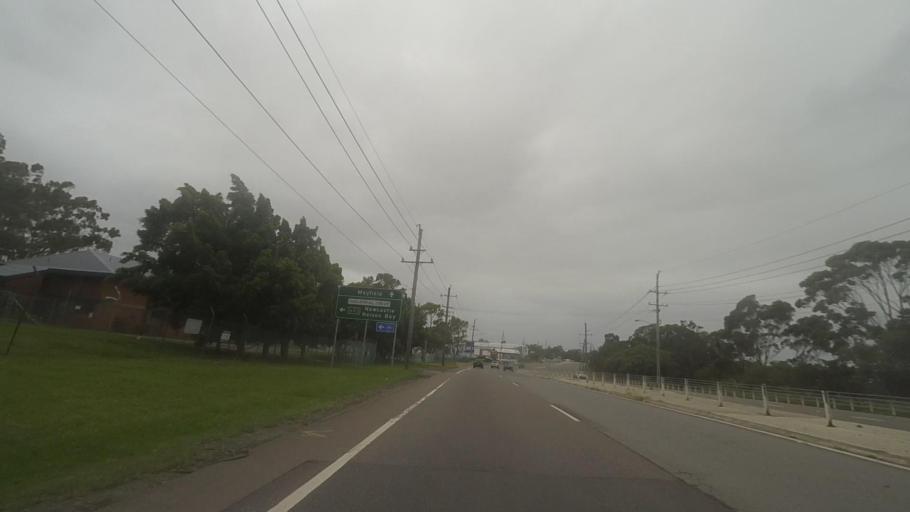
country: AU
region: New South Wales
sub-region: Newcastle
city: Mayfield West
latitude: -32.8794
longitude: 151.7166
